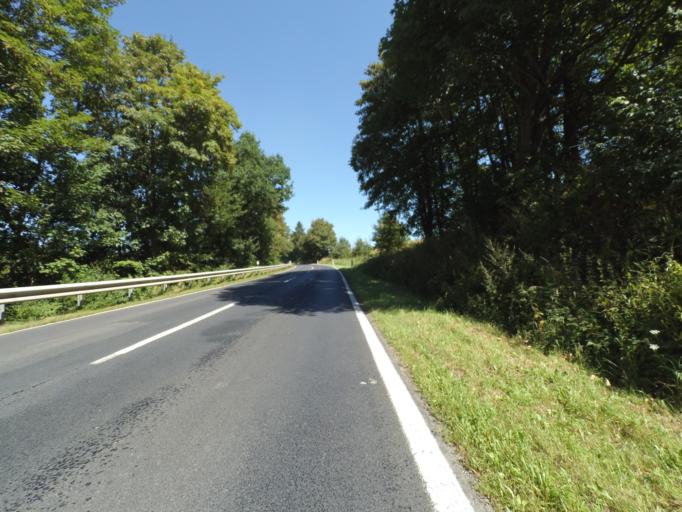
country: DE
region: Rheinland-Pfalz
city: Mullenbach
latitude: 50.2154
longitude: 7.0584
